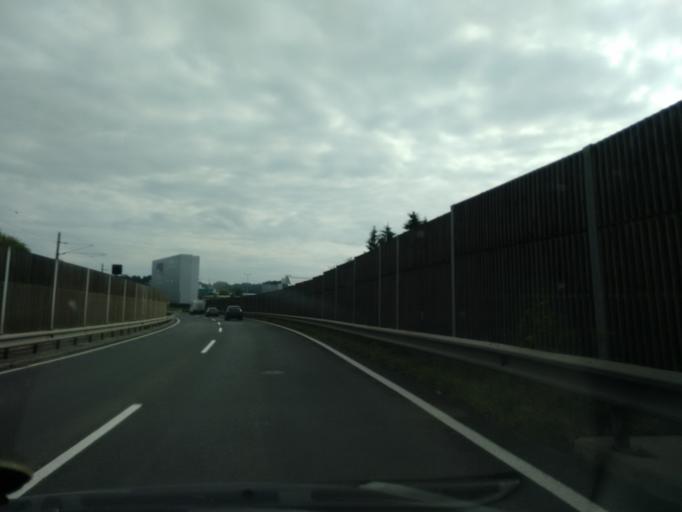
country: AT
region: Upper Austria
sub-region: Politischer Bezirk Vocklabruck
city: Lenzing
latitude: 47.9746
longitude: 13.6115
